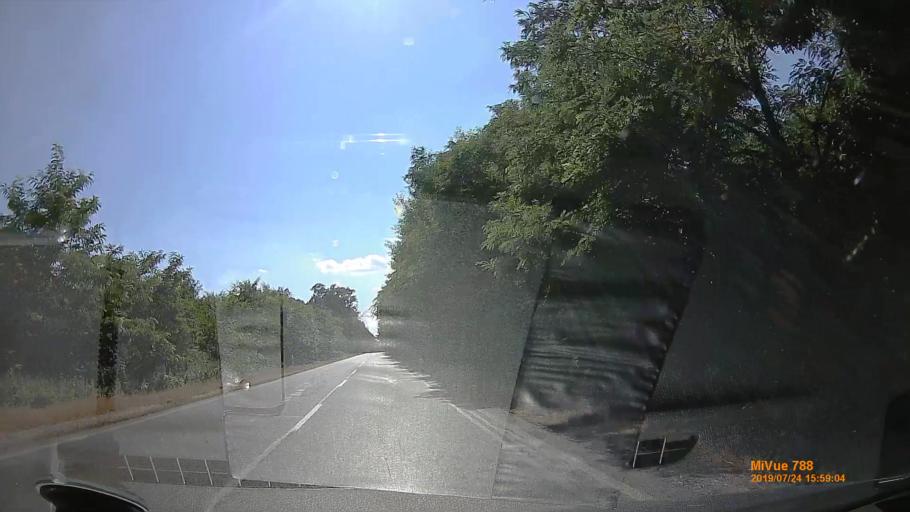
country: HU
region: Szabolcs-Szatmar-Bereg
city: Baktaloranthaza
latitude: 47.9798
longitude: 22.0468
